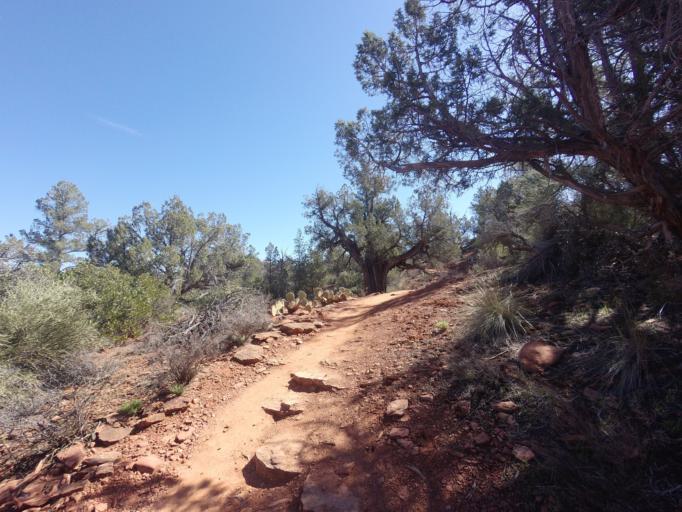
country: US
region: Arizona
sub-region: Yavapai County
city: West Sedona
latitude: 34.8066
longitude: -111.8264
